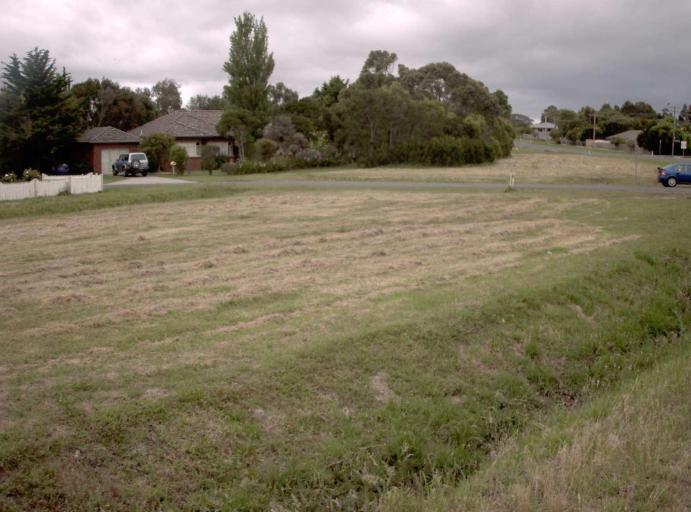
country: AU
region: Victoria
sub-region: Bass Coast
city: North Wonthaggi
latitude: -38.5950
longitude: 145.6068
